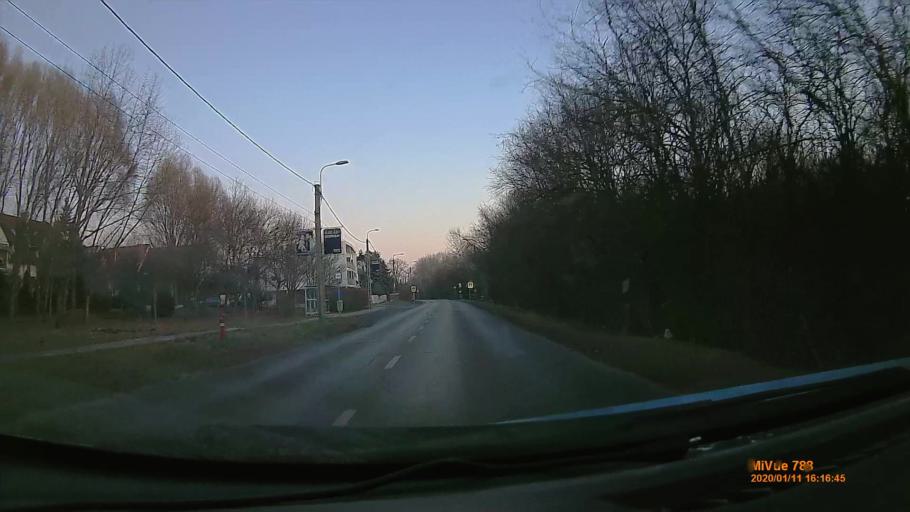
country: HU
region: Budapest
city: Budapest XVI. keruelet
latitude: 47.5251
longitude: 19.2040
